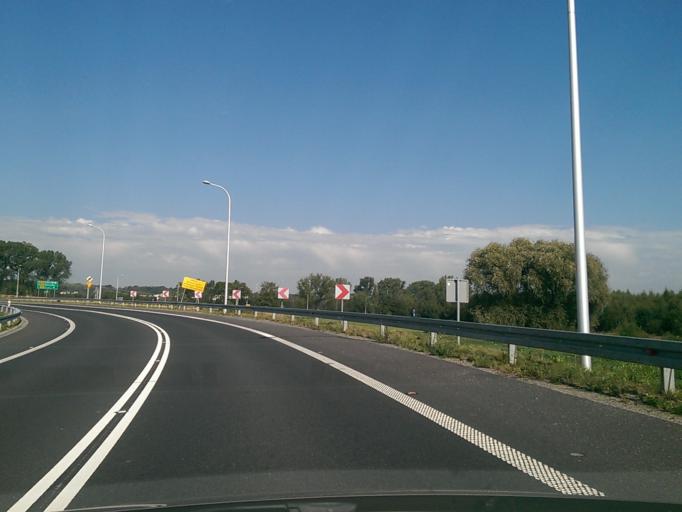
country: DE
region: Saxony
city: Zittau
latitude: 50.8997
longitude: 14.8482
